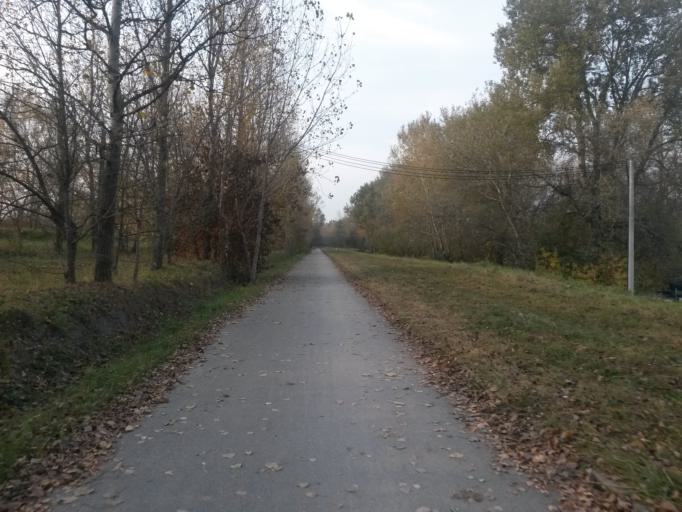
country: PL
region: Masovian Voivodeship
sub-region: Warszawa
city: Wawer
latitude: 52.1491
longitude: 21.1496
